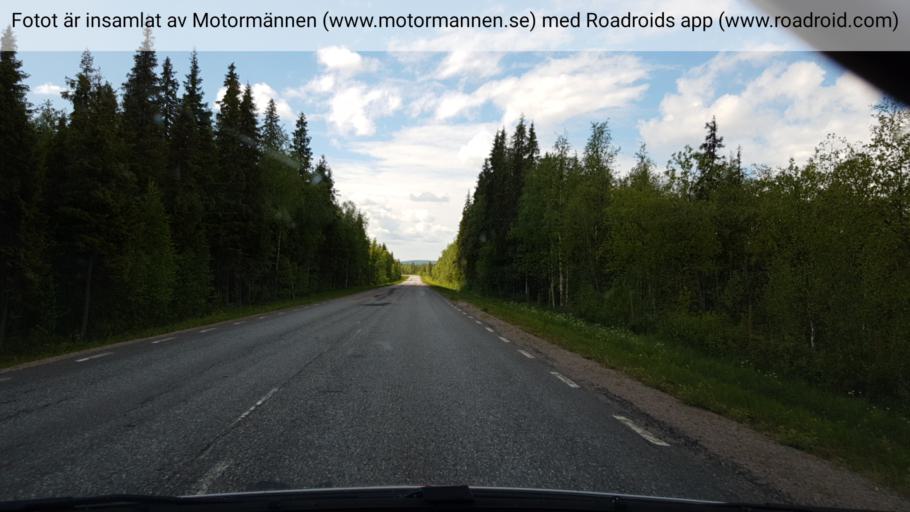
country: FI
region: Lapland
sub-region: Torniolaakso
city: Pello
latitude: 66.7696
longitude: 23.8767
